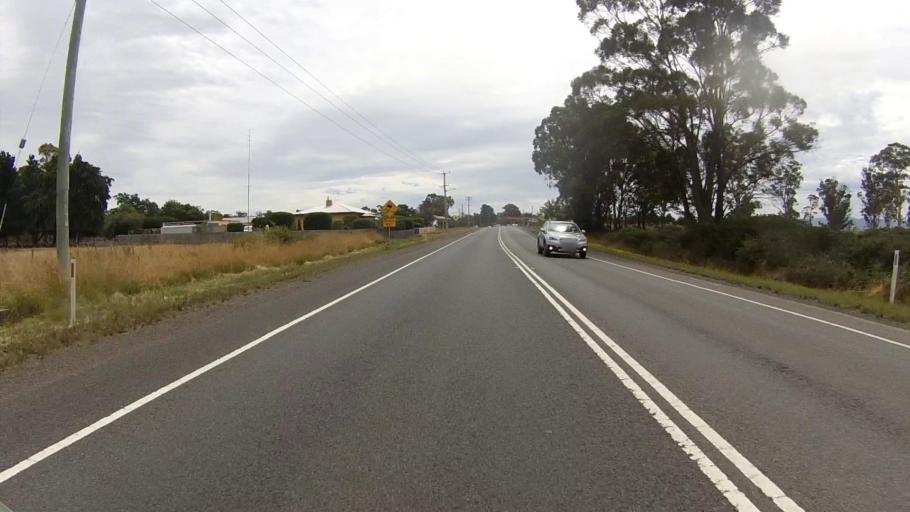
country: AU
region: Tasmania
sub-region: Northern Midlands
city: Evandale
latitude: -41.7623
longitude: 147.3530
